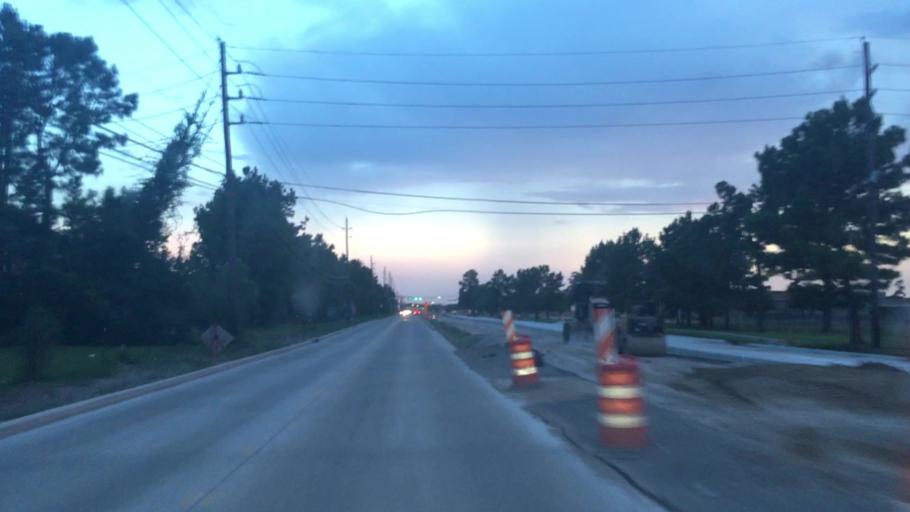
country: US
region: Texas
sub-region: Harris County
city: Humble
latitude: 29.9469
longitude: -95.2497
